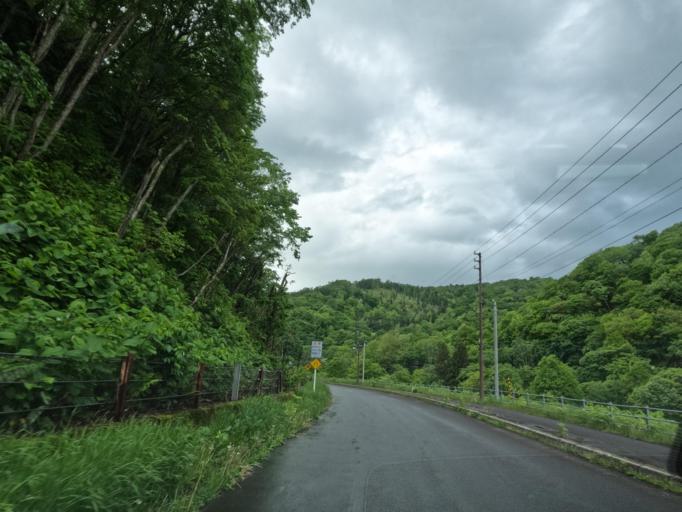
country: JP
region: Hokkaido
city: Fukagawa
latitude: 43.7306
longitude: 142.2029
